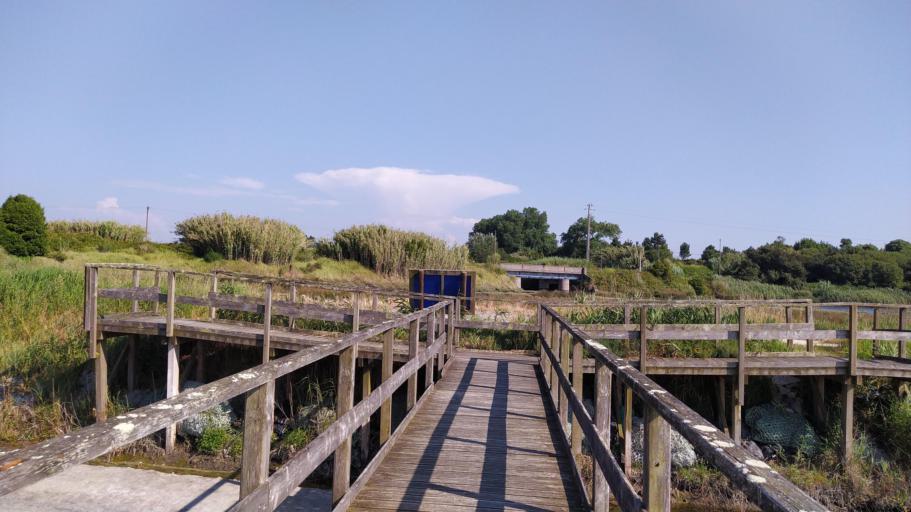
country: PT
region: Aveiro
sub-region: Aveiro
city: Aradas
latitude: 40.6285
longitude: -8.6615
